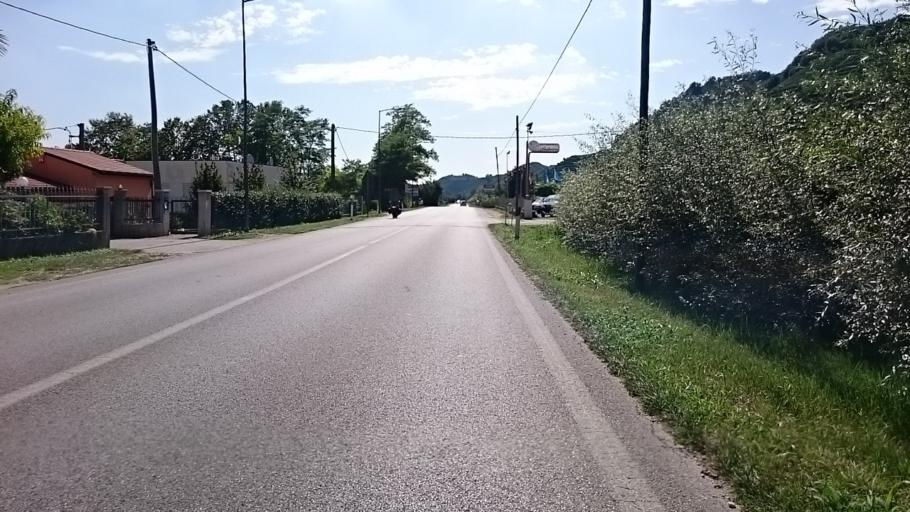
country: IT
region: Veneto
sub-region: Provincia di Treviso
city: Mosnigo
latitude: 45.8902
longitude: 12.0691
